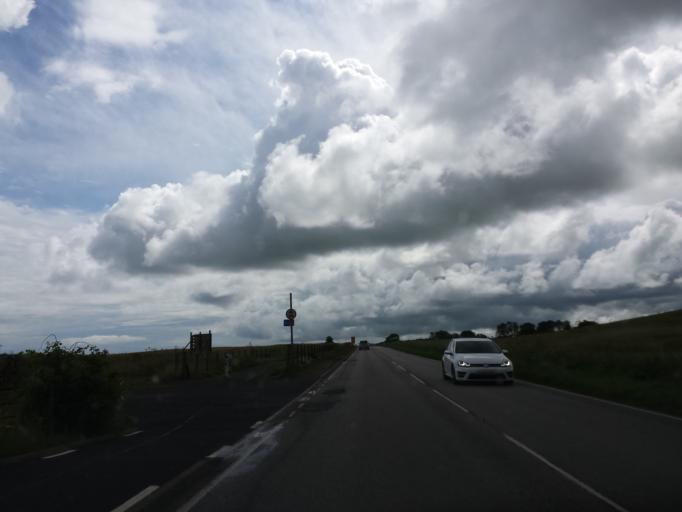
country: GB
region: Scotland
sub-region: Fife
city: Strathkinness
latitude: 56.3583
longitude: -2.8658
